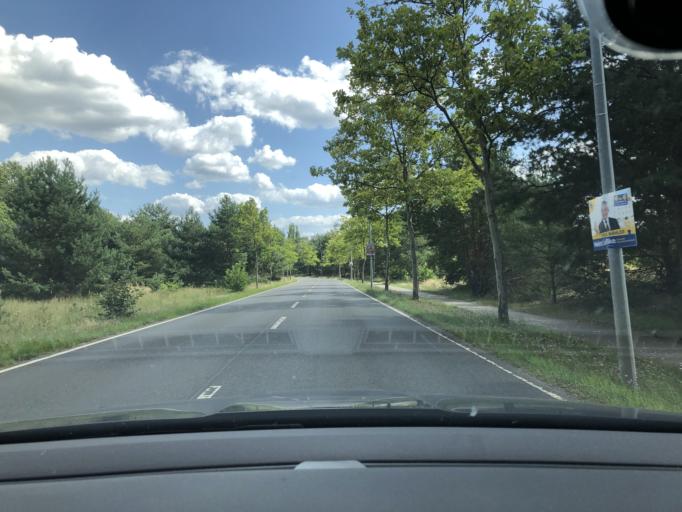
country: DE
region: Brandenburg
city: Oranienburg
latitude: 52.7719
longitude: 13.2551
